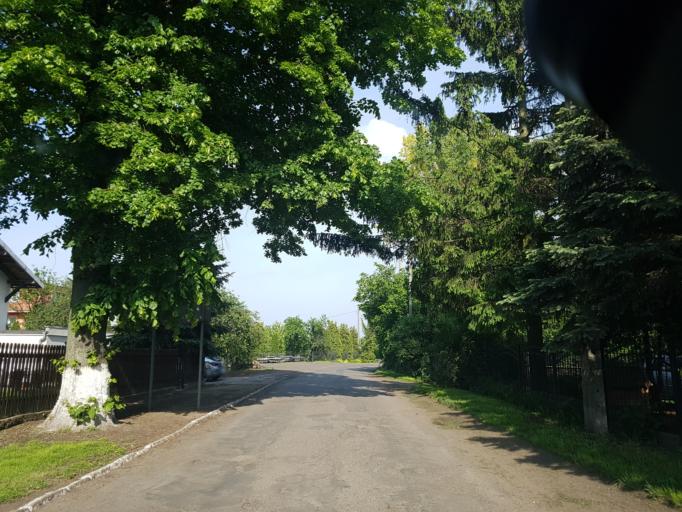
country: PL
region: Lower Silesian Voivodeship
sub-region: Powiat strzelinski
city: Wiazow
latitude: 50.8662
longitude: 17.1573
